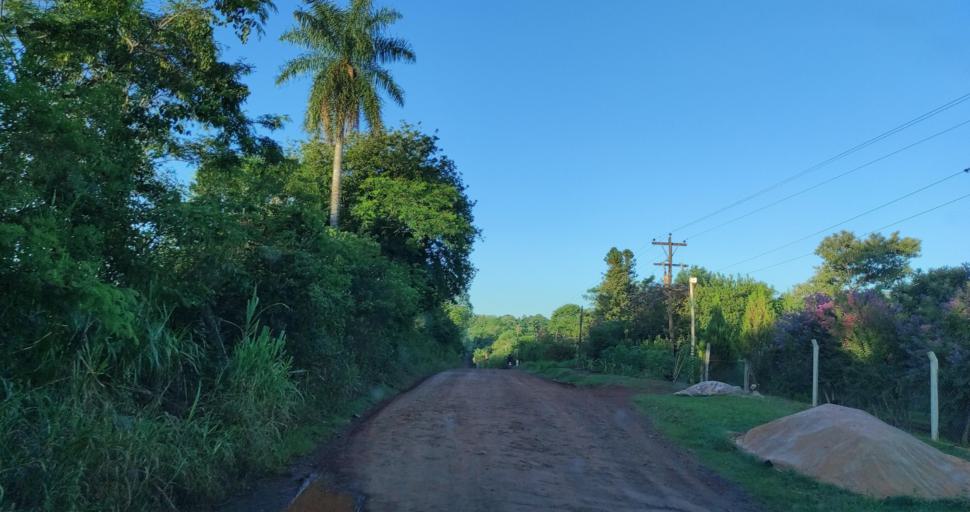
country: AR
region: Misiones
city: Gobernador Roca
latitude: -27.2212
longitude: -55.4278
